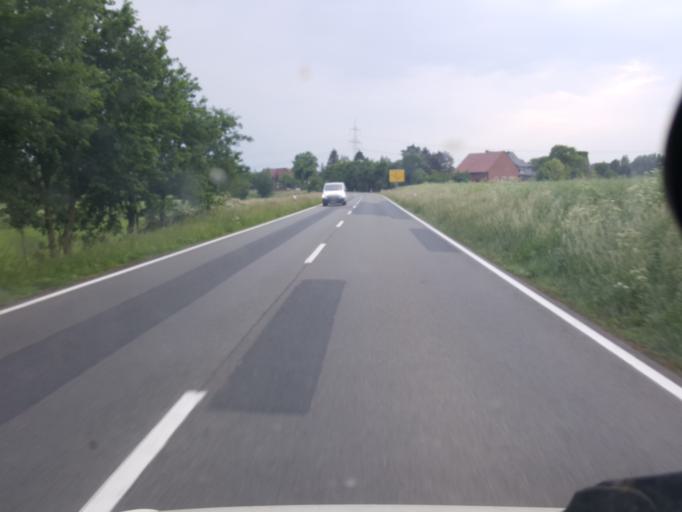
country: DE
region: Lower Saxony
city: Raddestorf
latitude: 52.4666
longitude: 8.9767
